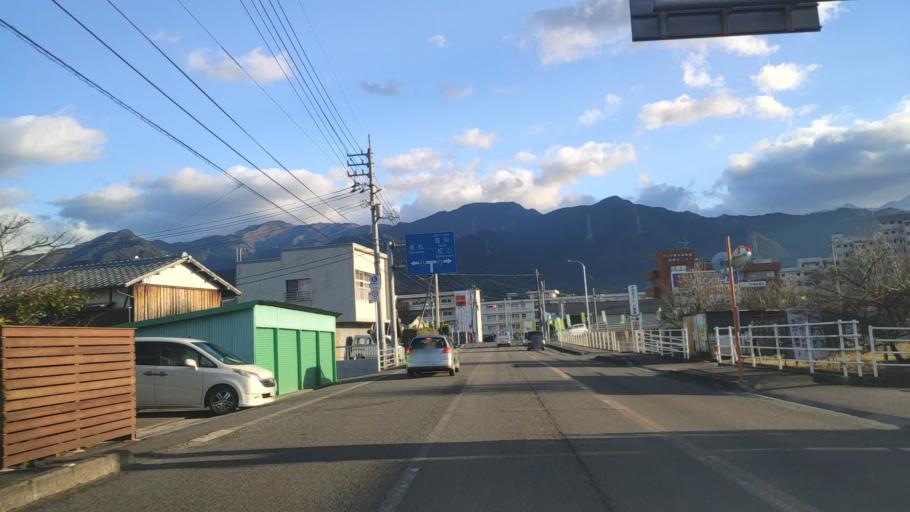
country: JP
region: Ehime
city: Saijo
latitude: 33.9066
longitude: 133.1857
